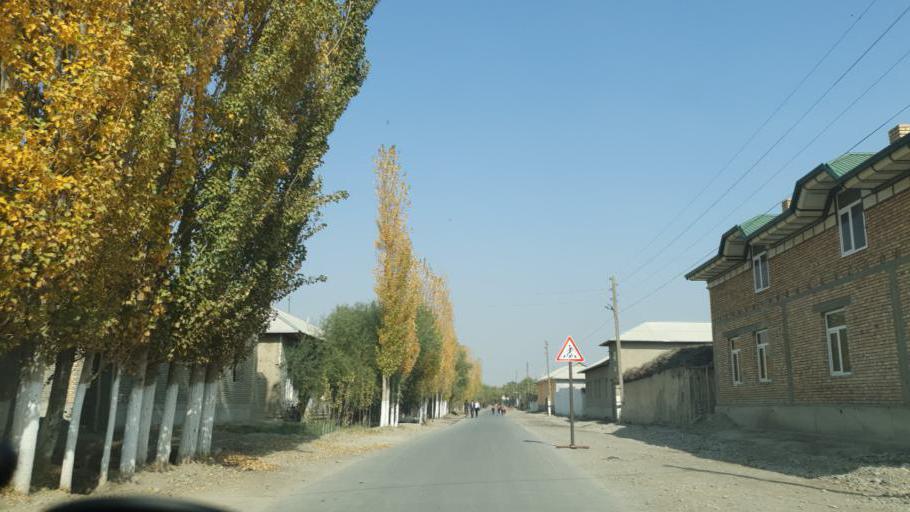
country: UZ
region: Fergana
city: Beshariq
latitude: 40.4928
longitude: 70.6212
